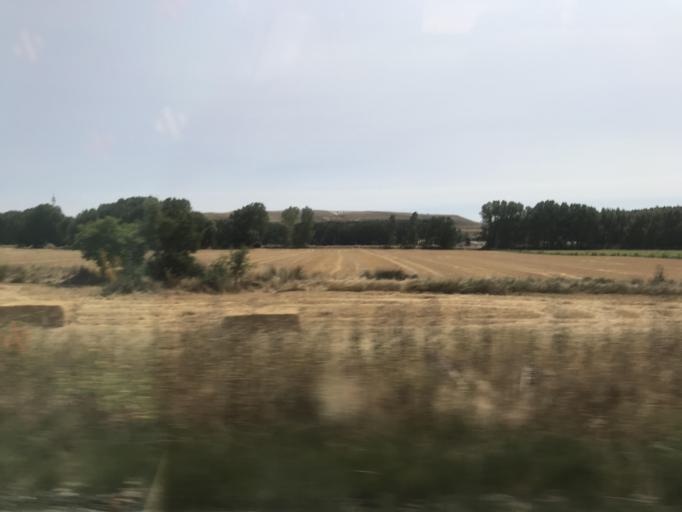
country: ES
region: Castille and Leon
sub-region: Provincia de Burgos
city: Frandovinez
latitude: 42.2883
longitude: -3.8558
